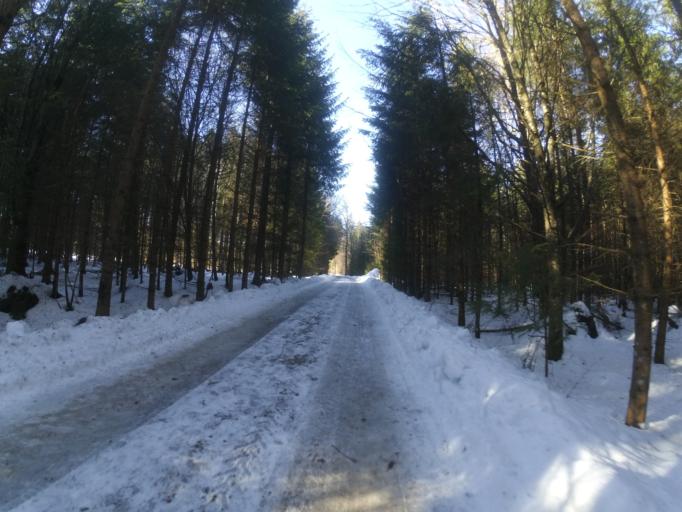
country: DE
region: Bavaria
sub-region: Upper Bavaria
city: Aying
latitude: 47.9831
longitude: 11.7586
